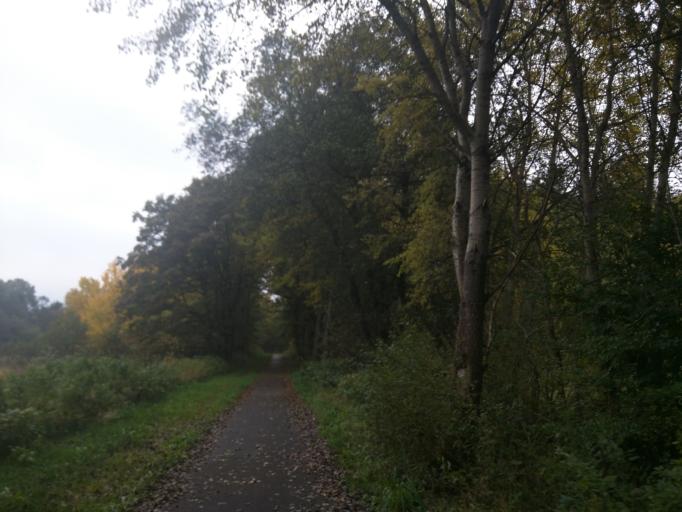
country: DK
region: Central Jutland
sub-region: Silkeborg Kommune
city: Silkeborg
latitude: 56.2392
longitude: 9.5286
